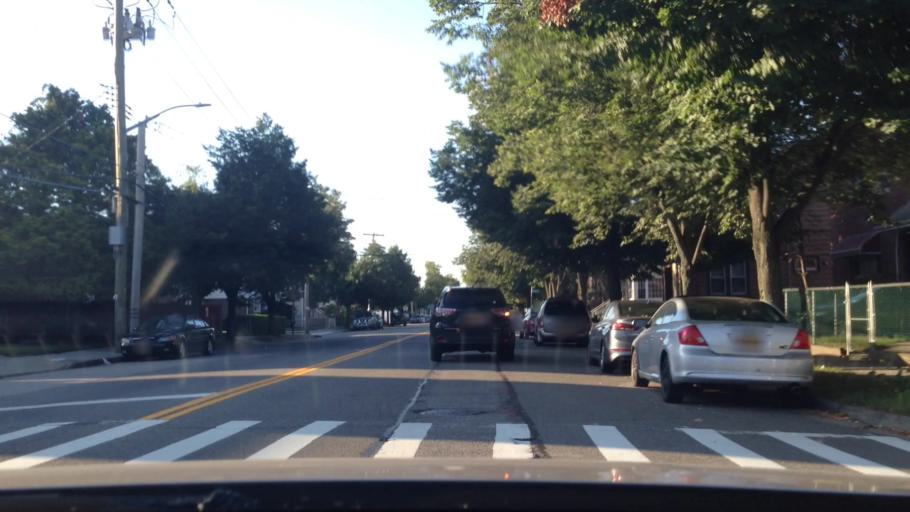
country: US
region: New York
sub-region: Nassau County
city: South Valley Stream
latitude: 40.6626
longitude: -73.7330
